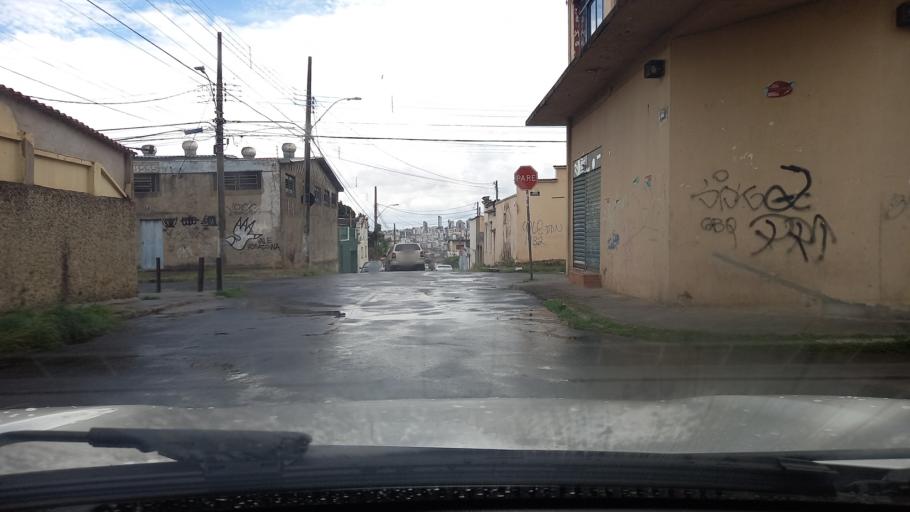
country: BR
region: Minas Gerais
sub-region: Belo Horizonte
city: Belo Horizonte
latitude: -19.9065
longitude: -43.9513
